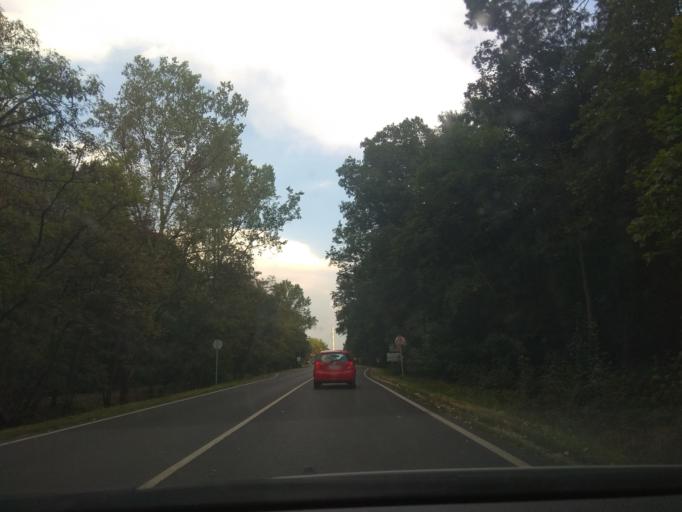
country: HU
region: Borsod-Abauj-Zemplen
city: Sajooeroes
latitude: 47.9293
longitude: 21.0281
